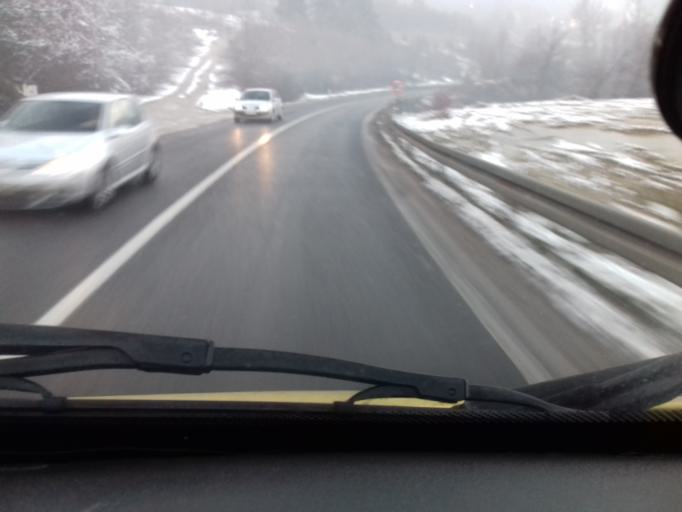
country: BA
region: Federation of Bosnia and Herzegovina
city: Vogosca
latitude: 43.8932
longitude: 18.3203
